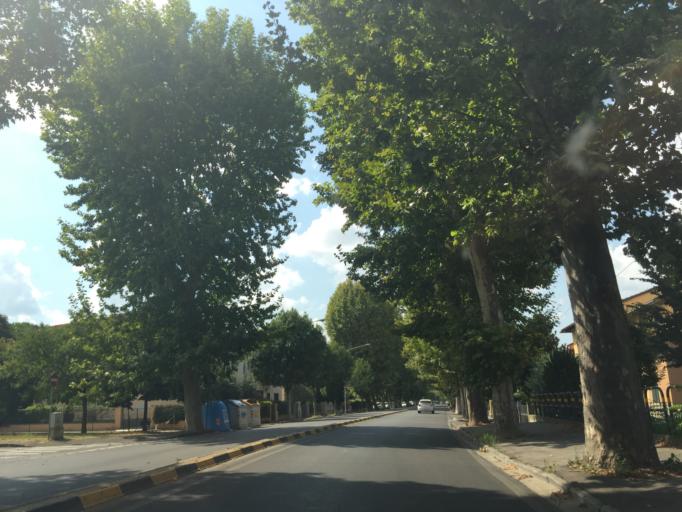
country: IT
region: Tuscany
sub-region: Province of Florence
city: Mantignano-Ugnano
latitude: 43.7928
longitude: 11.1659
